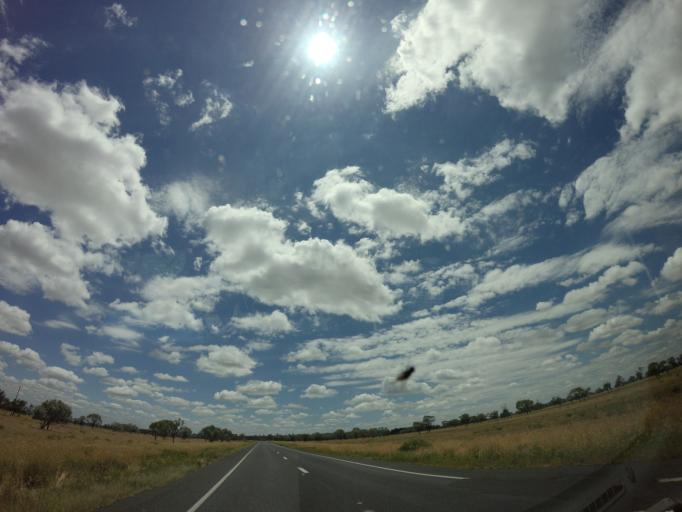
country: AU
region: New South Wales
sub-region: Moree Plains
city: Boggabilla
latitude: -28.9265
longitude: 150.1199
